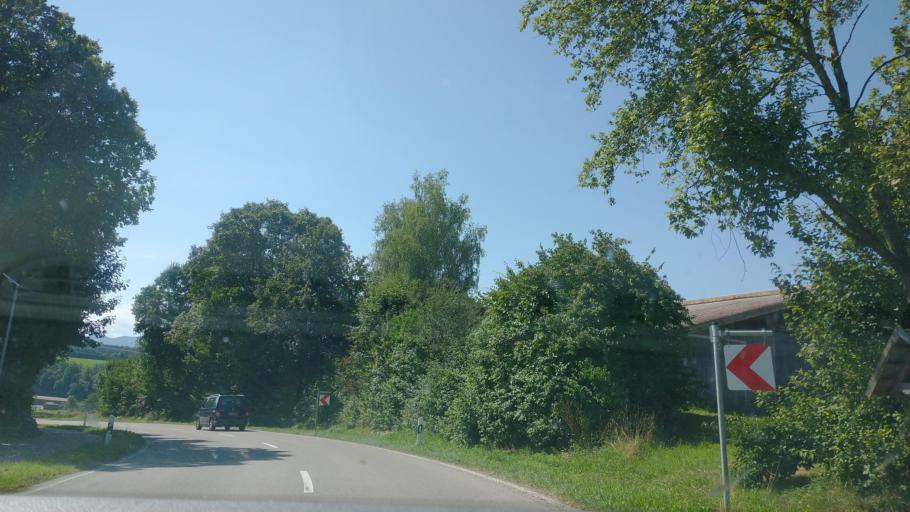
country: DE
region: Bavaria
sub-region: Swabia
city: Hergensweiler
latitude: 47.6559
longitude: 9.7748
